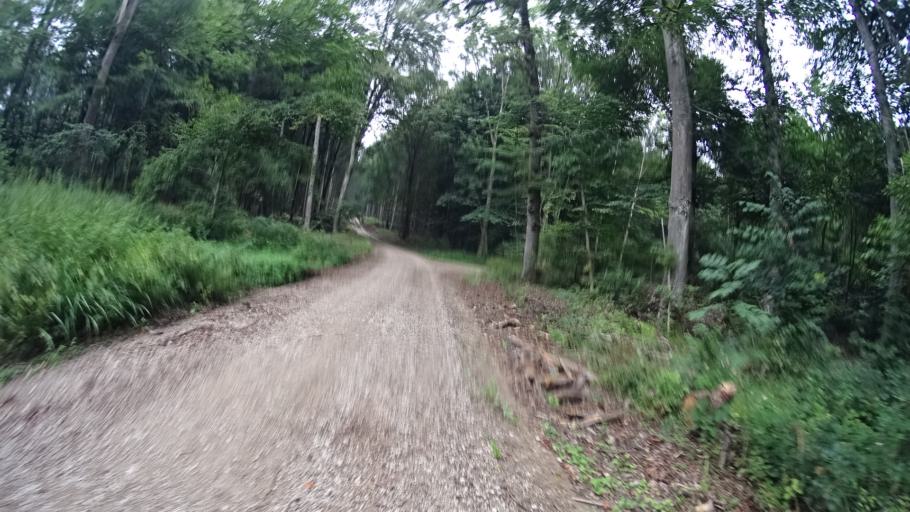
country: DE
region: Bavaria
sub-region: Upper Bavaria
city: Stammham
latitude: 48.8402
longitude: 11.4858
